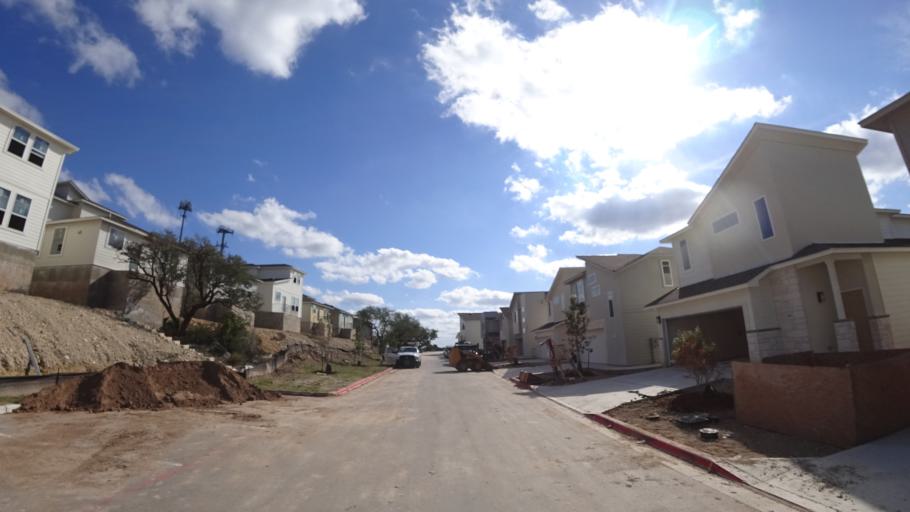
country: US
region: Texas
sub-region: Travis County
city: Barton Creek
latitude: 30.2444
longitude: -97.8776
